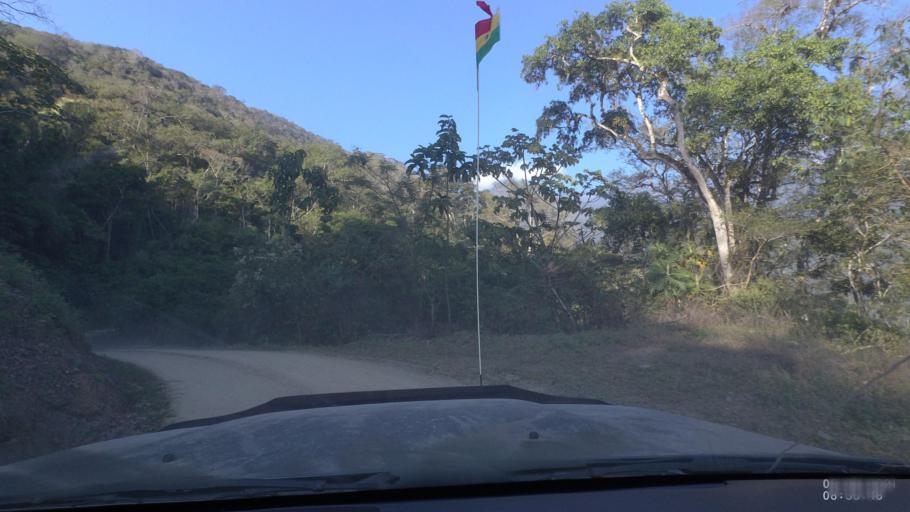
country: BO
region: La Paz
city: Quime
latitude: -16.5112
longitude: -66.7630
